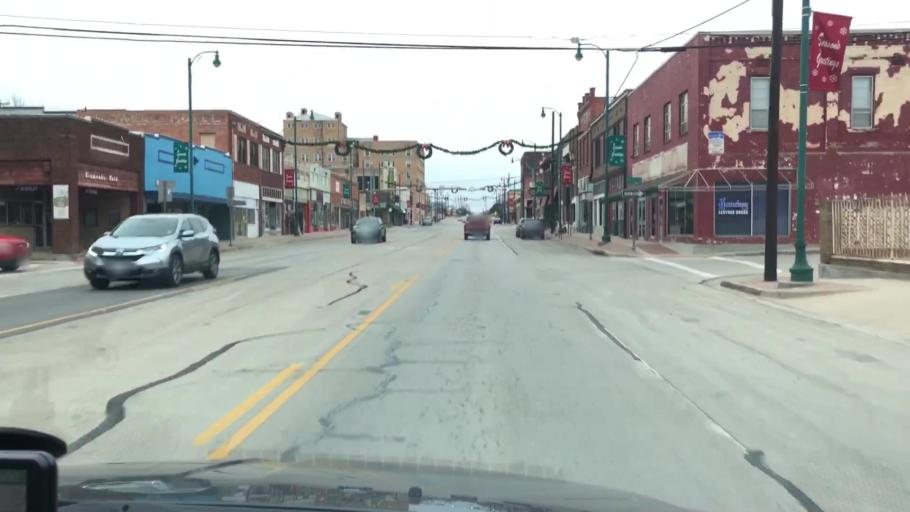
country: US
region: Texas
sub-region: Palo Pinto County
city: Mineral Wells
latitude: 32.8097
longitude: -98.1129
